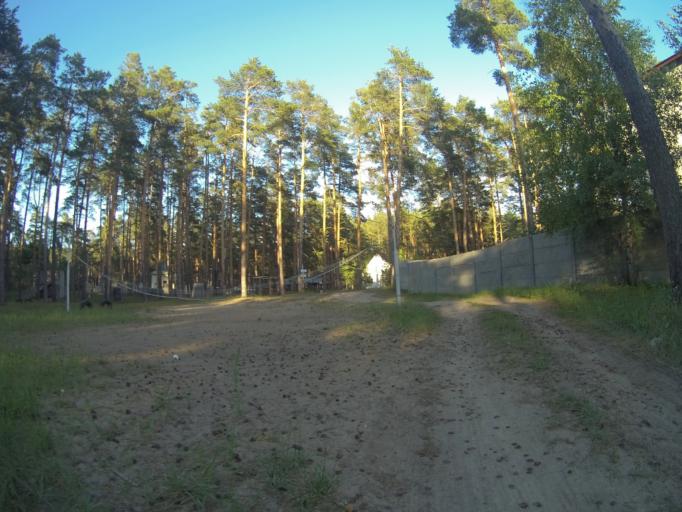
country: RU
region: Vladimir
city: Kommunar
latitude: 56.1422
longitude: 40.4900
